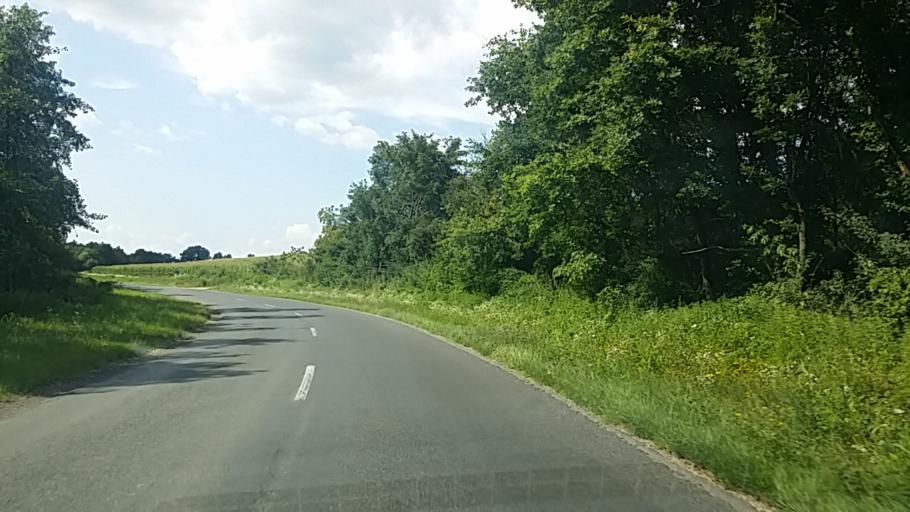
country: HU
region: Zala
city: Becsehely
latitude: 46.4853
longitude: 16.7919
